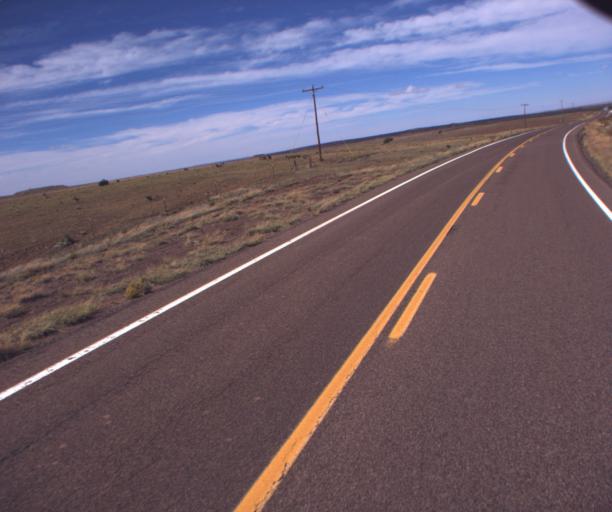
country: US
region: Arizona
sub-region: Apache County
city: Saint Johns
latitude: 34.4835
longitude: -109.6190
